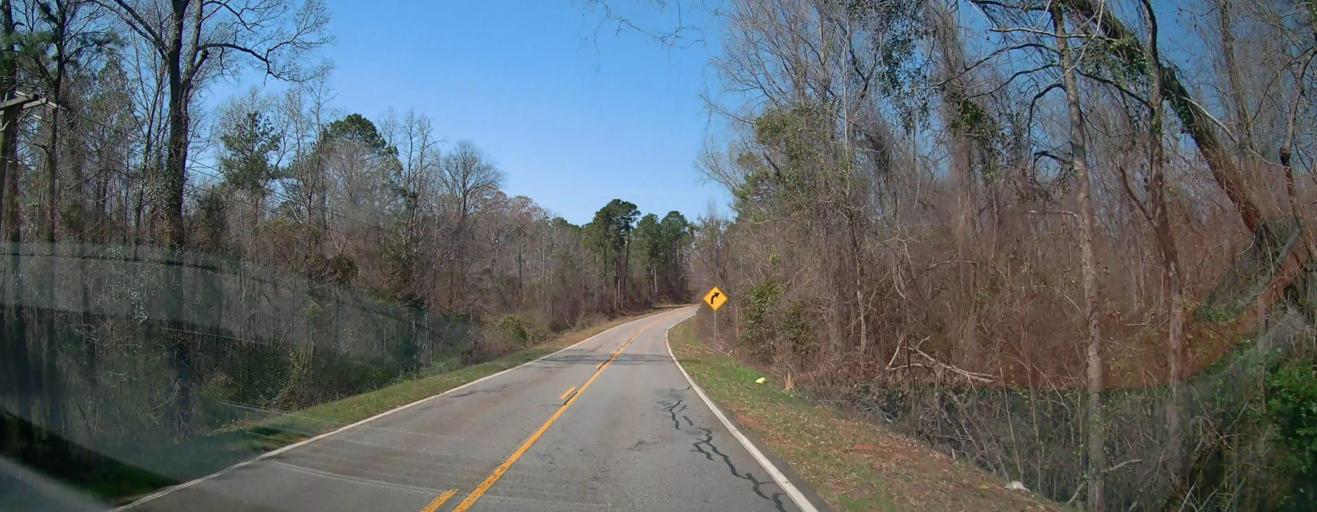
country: US
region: Georgia
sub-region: Peach County
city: Byron
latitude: 32.5811
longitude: -83.7583
